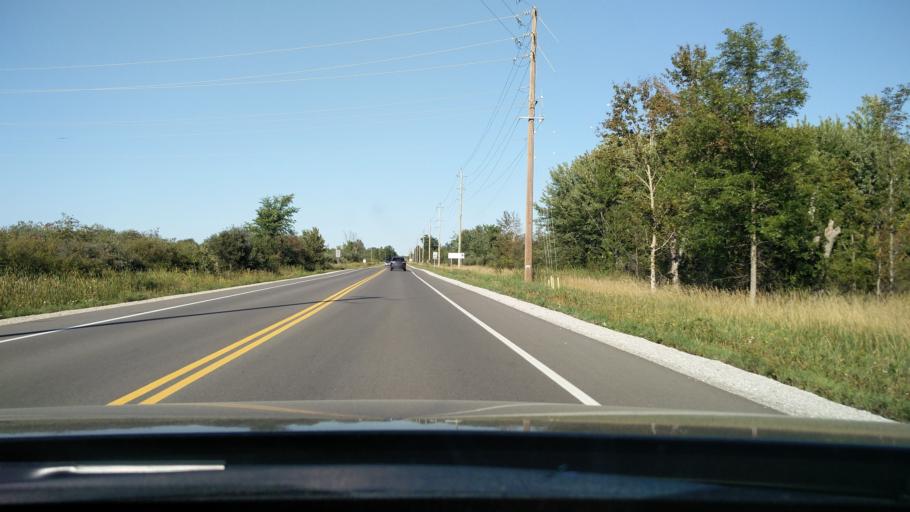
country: CA
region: Ontario
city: Perth
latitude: 44.9081
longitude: -76.2415
